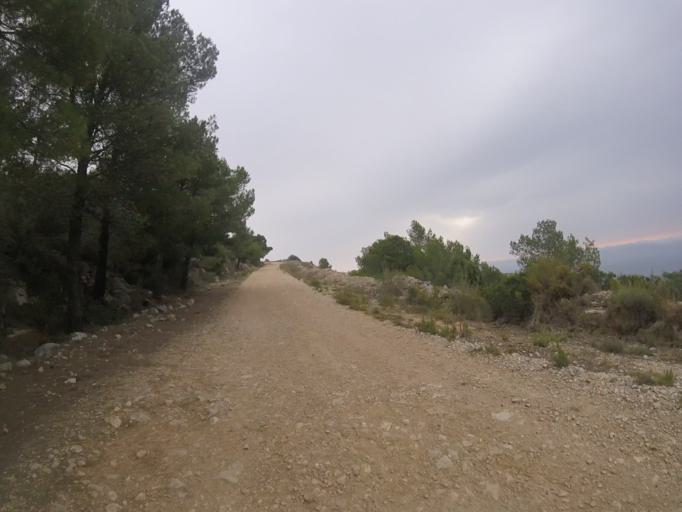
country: ES
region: Valencia
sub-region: Provincia de Castello
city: Alcoceber
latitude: 40.2781
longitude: 0.2826
